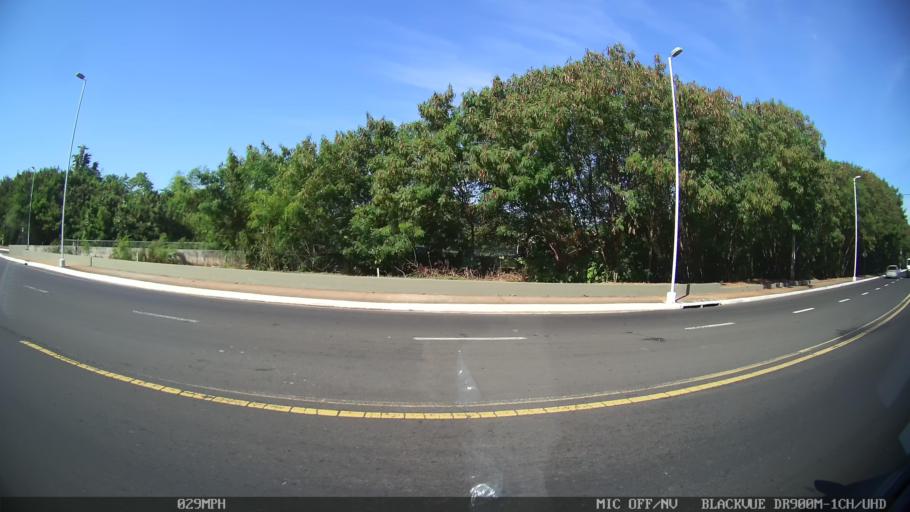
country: BR
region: Sao Paulo
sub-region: Sao Jose Do Rio Preto
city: Sao Jose do Rio Preto
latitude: -20.8011
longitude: -49.4072
